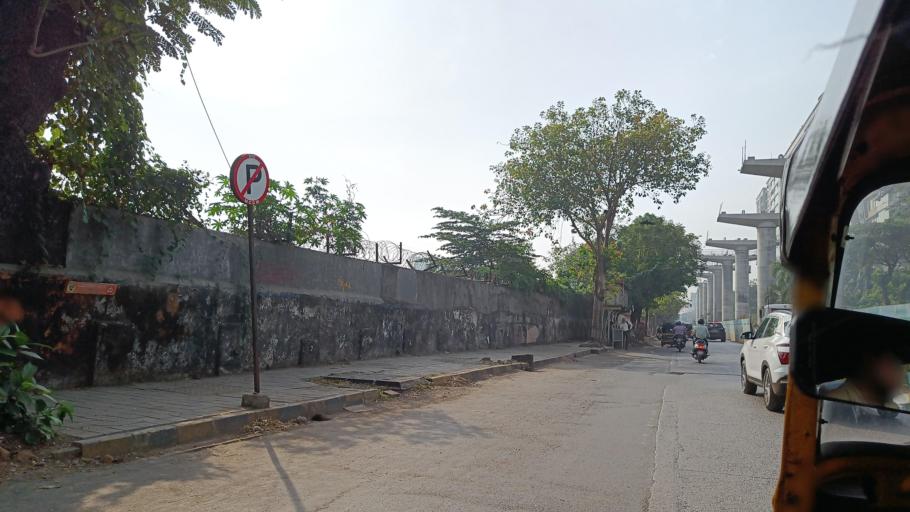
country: IN
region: Maharashtra
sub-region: Mumbai Suburban
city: Mumbai
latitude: 19.1213
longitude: 72.8300
